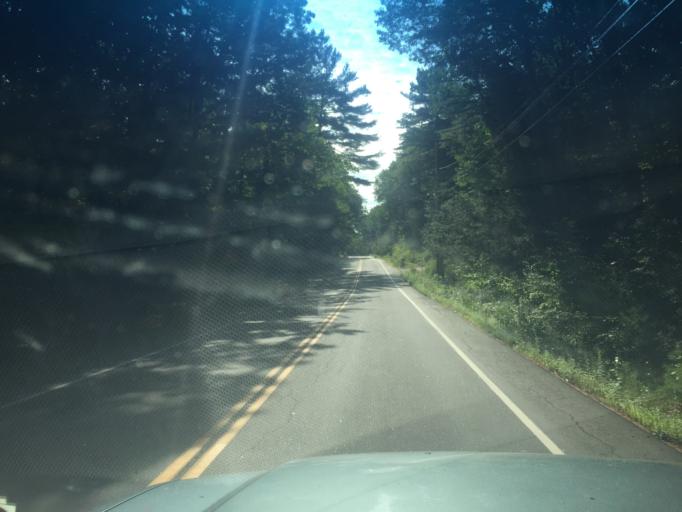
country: US
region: Maine
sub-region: York County
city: South Berwick
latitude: 43.2037
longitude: -70.7729
